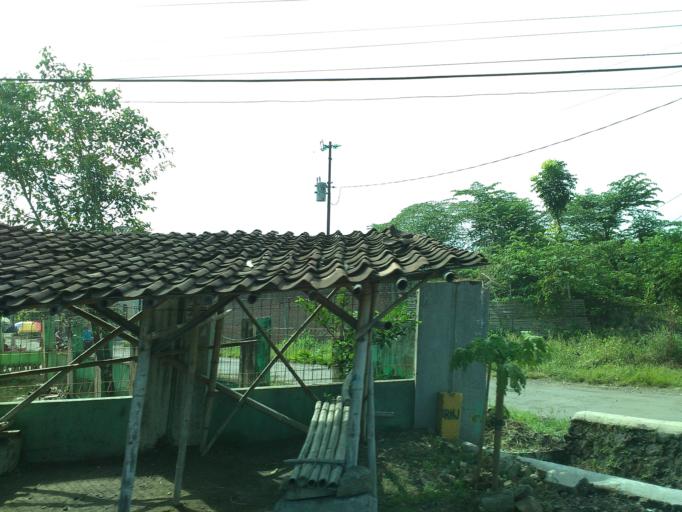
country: ID
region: Central Java
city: Ceper
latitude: -7.6627
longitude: 110.6697
